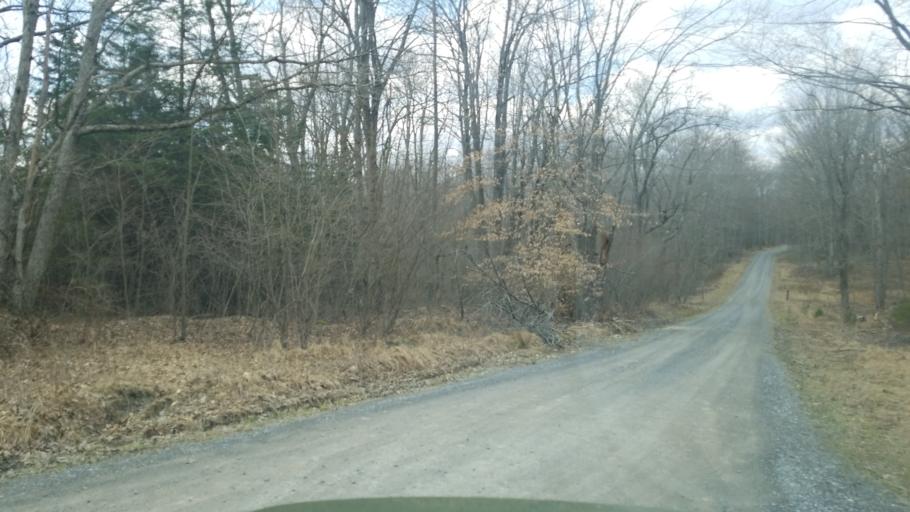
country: US
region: Pennsylvania
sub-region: Clearfield County
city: Clearfield
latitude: 41.1736
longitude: -78.4891
